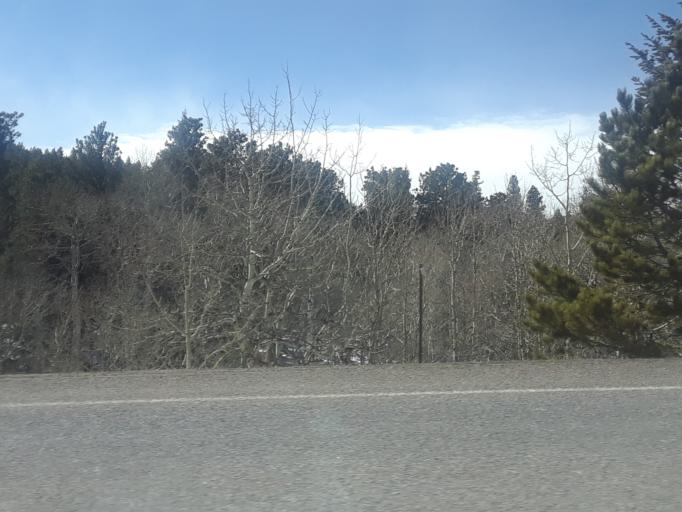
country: US
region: Colorado
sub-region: Boulder County
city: Nederland
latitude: 40.0006
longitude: -105.5033
